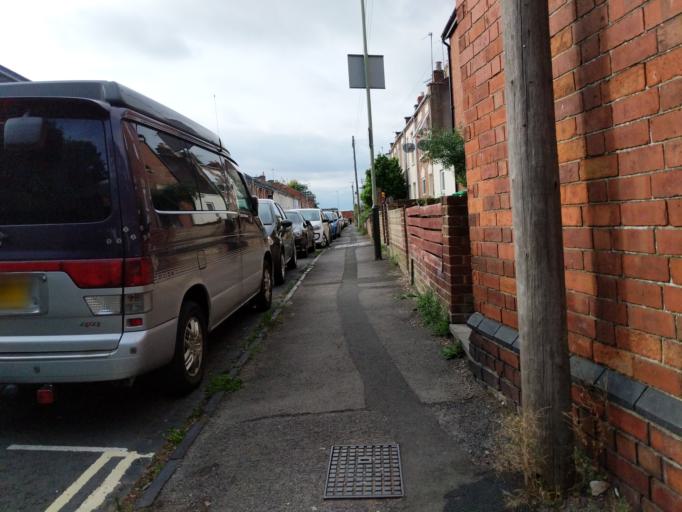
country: GB
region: England
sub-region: Gloucestershire
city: Cheltenham
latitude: 51.9039
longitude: -2.0855
